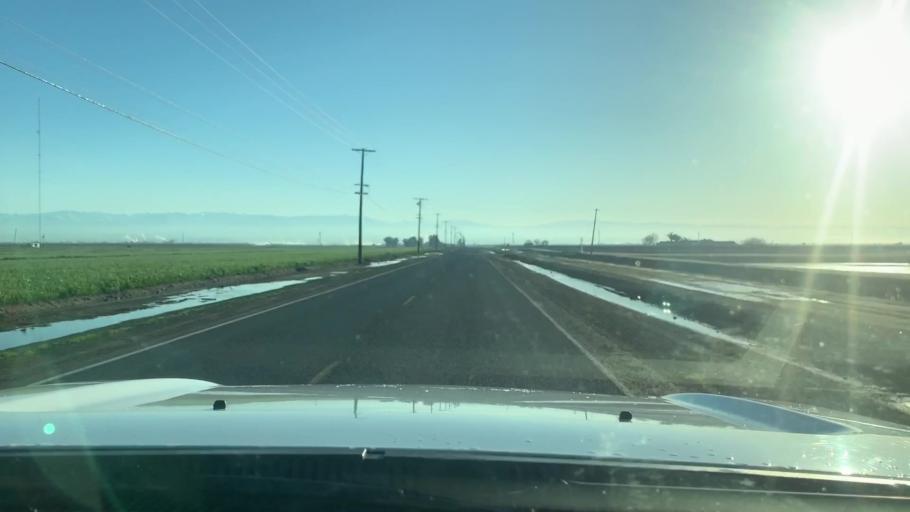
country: US
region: California
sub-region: Tulare County
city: Tulare
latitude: 36.1817
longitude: -119.4085
